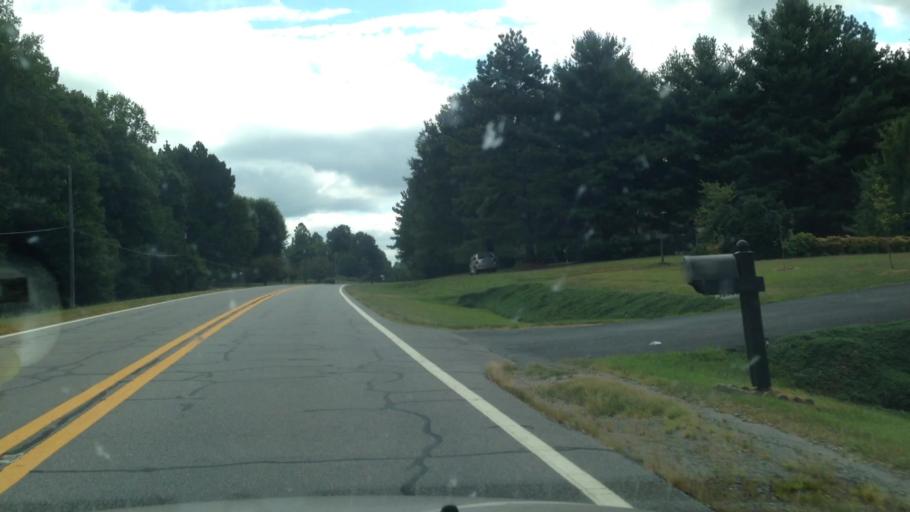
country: US
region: North Carolina
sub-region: Rockingham County
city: Wentworth
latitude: 36.3860
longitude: -79.8236
